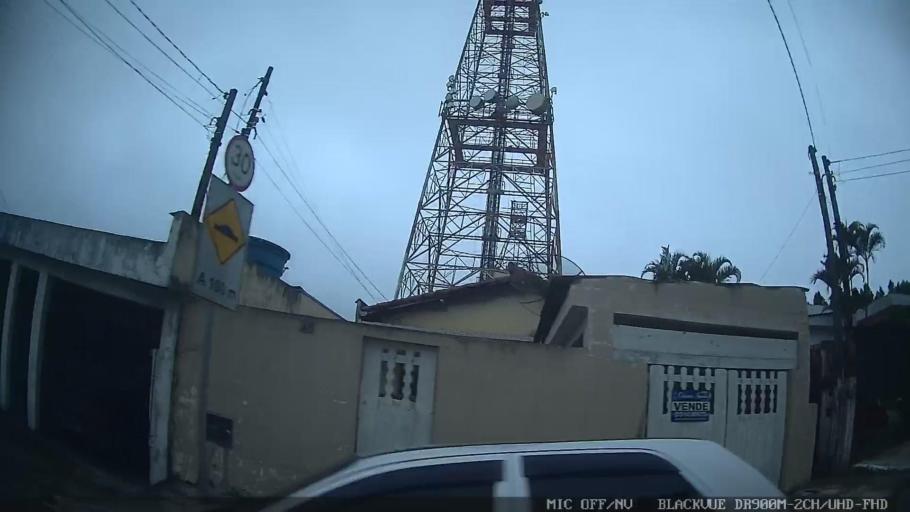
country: BR
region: Sao Paulo
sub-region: Mogi das Cruzes
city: Mogi das Cruzes
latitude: -23.5107
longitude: -46.1495
